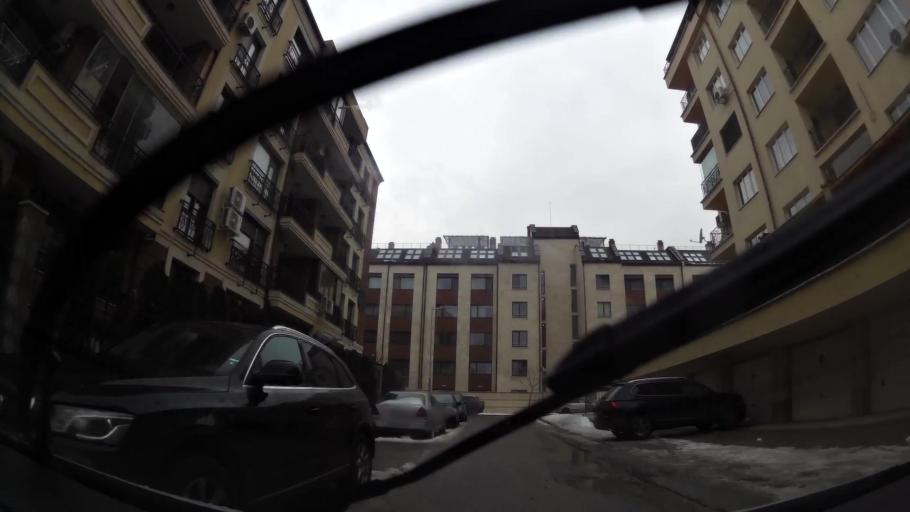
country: BG
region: Sofia-Capital
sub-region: Stolichna Obshtina
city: Sofia
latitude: 42.6615
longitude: 23.2904
